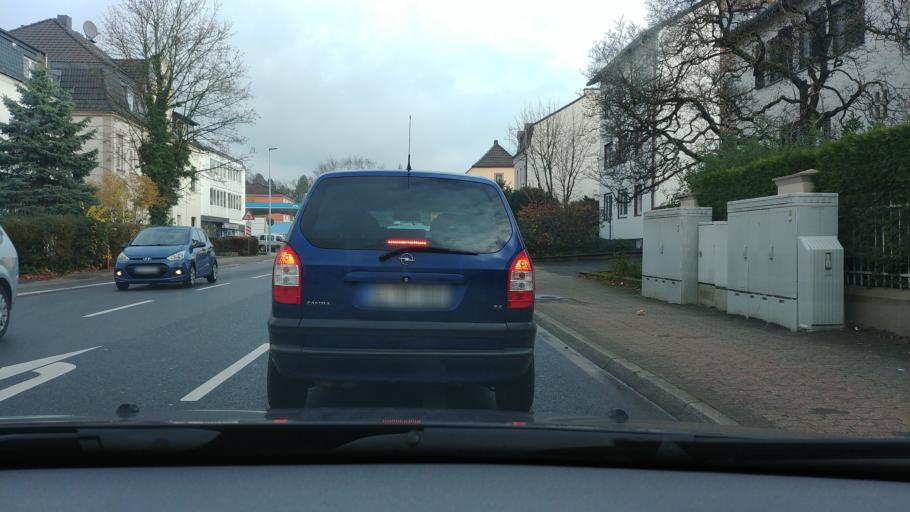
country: DE
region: North Rhine-Westphalia
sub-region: Regierungsbezirk Koln
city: Bergisch Gladbach
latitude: 50.9607
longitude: 7.1465
